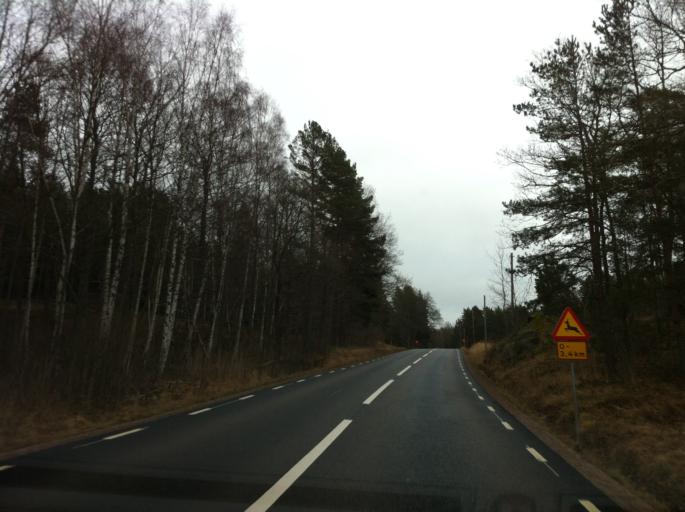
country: SE
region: Kalmar
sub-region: Vasterviks Kommun
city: Overum
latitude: 57.9104
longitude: 16.2003
